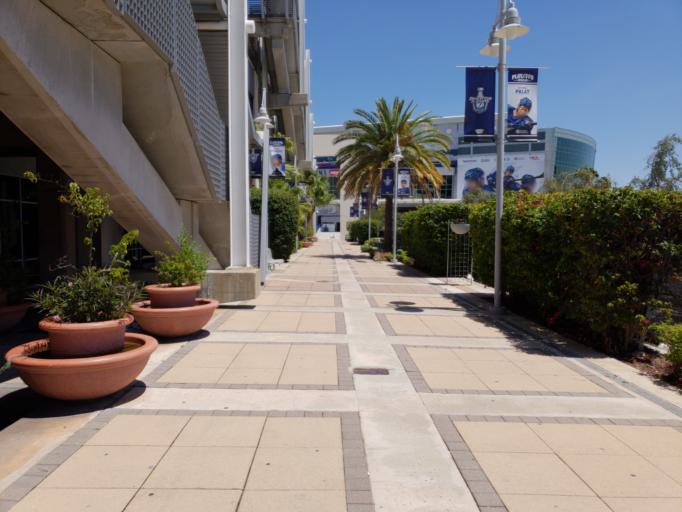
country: US
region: Florida
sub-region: Hillsborough County
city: Tampa
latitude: 27.9422
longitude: -82.4539
